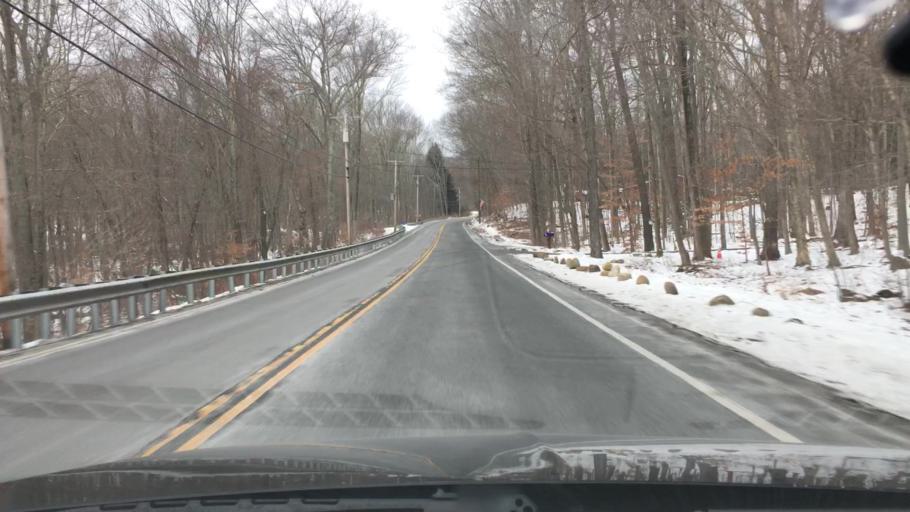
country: US
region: Connecticut
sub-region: Tolland County
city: Tolland
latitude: 41.8464
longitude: -72.3256
